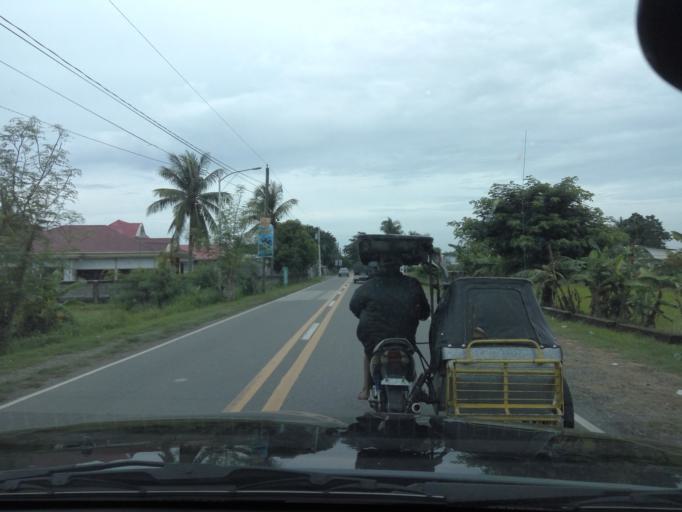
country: PH
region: Central Luzon
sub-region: Province of Nueva Ecija
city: Carmen
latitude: 15.4458
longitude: 120.8294
